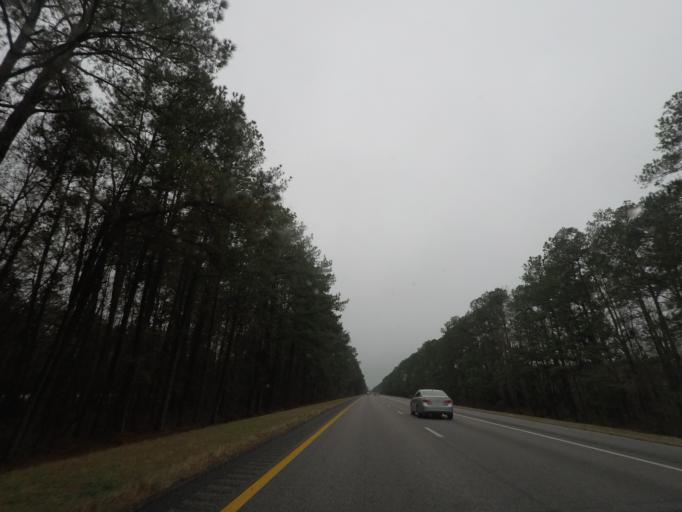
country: US
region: South Carolina
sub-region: Sumter County
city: East Sumter
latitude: 33.9292
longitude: -80.0711
